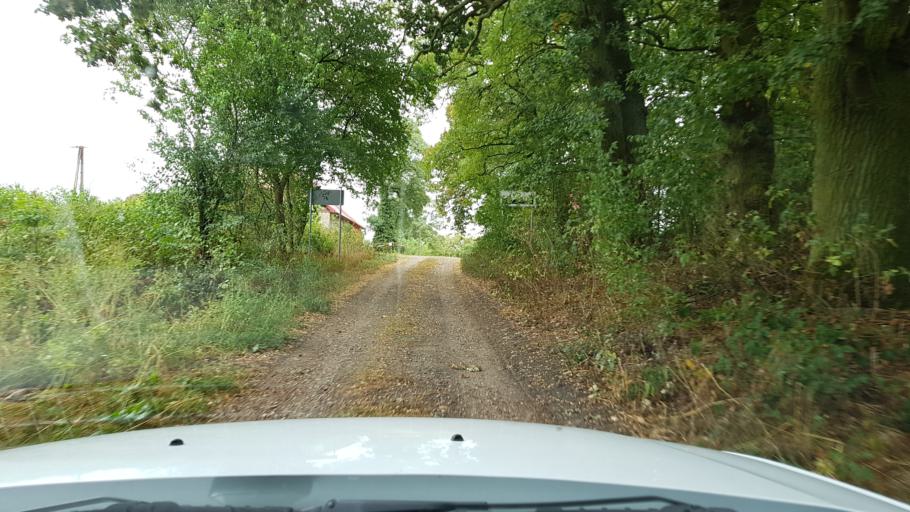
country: PL
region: West Pomeranian Voivodeship
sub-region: Powiat gryfinski
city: Chojna
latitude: 52.8974
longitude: 14.4529
